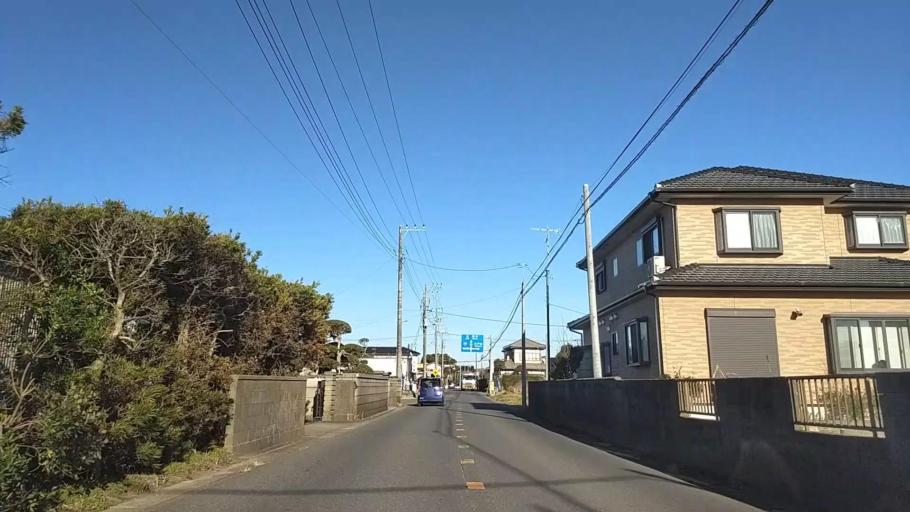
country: JP
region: Chiba
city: Yokaichiba
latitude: 35.6187
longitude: 140.5372
